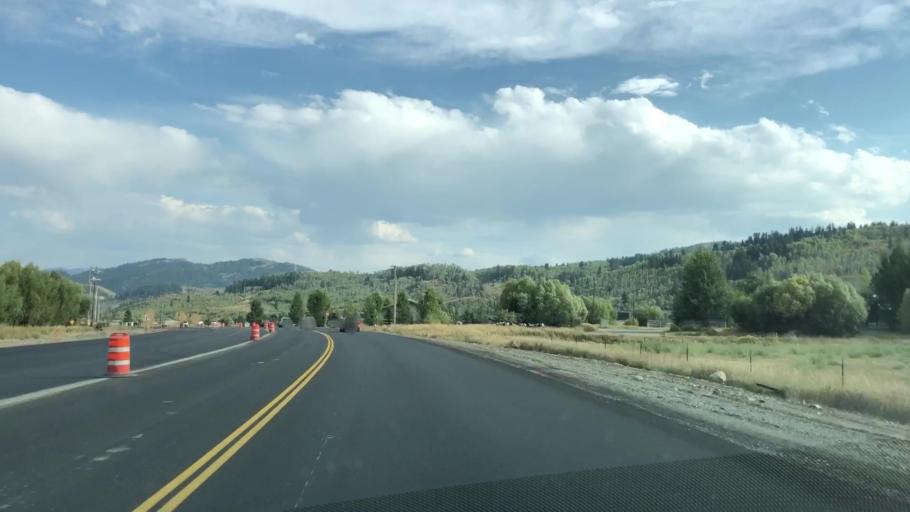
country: US
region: Wyoming
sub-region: Teton County
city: South Park
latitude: 43.3739
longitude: -110.7442
